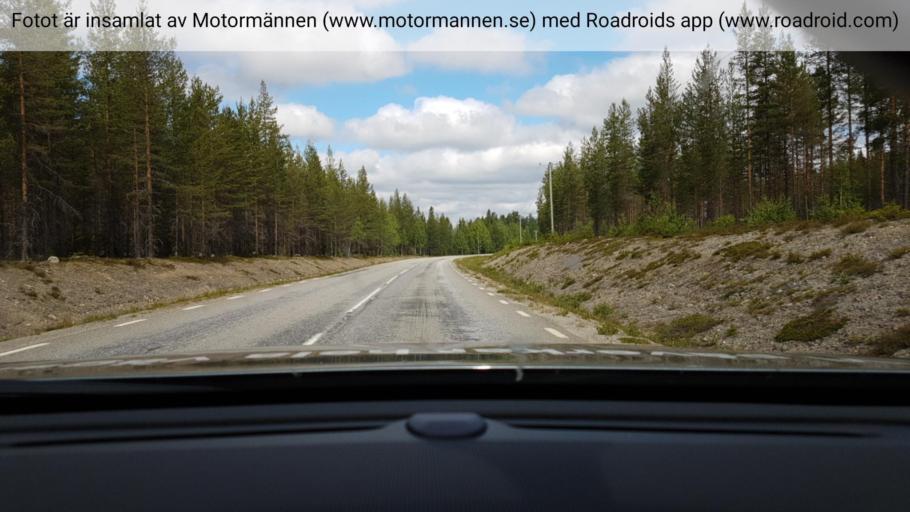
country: SE
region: Vaesterbotten
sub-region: Lycksele Kommun
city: Lycksele
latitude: 64.8592
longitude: 18.7280
